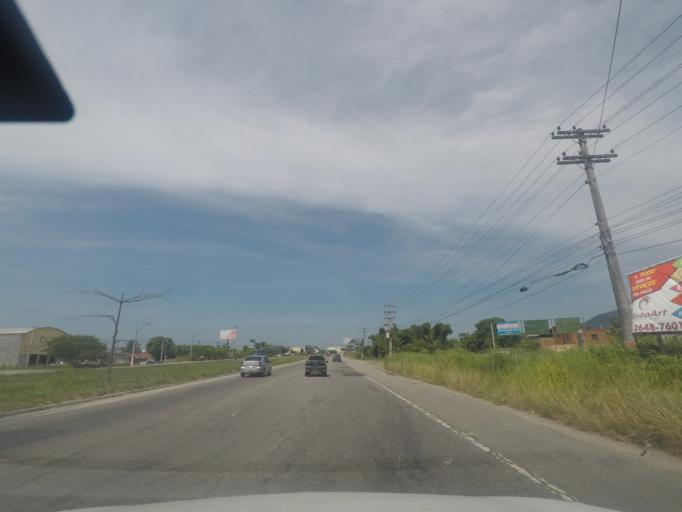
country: BR
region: Rio de Janeiro
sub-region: Marica
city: Marica
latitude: -22.9060
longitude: -42.8168
